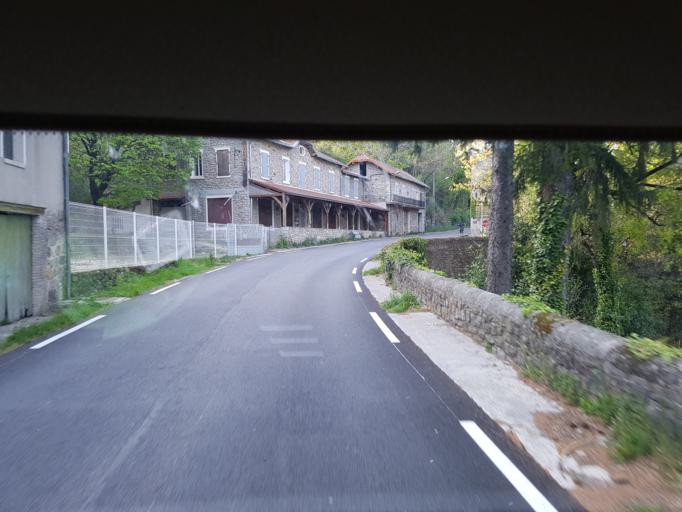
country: FR
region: Languedoc-Roussillon
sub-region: Departement du Gard
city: Branoux-les-Taillades
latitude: 44.3474
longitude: 3.9486
